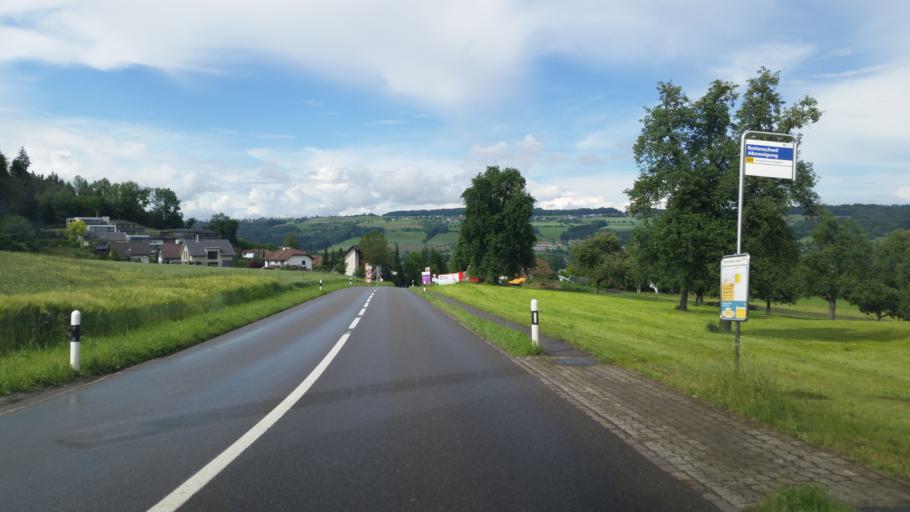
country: CH
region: Aargau
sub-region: Bezirk Muri
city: Aristau
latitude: 47.3083
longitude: 8.3579
